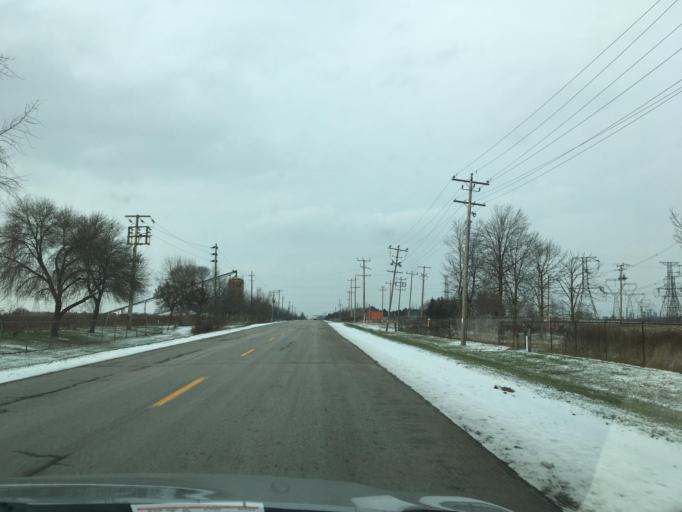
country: CA
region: Ontario
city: Norfolk County
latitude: 42.8001
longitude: -80.0586
